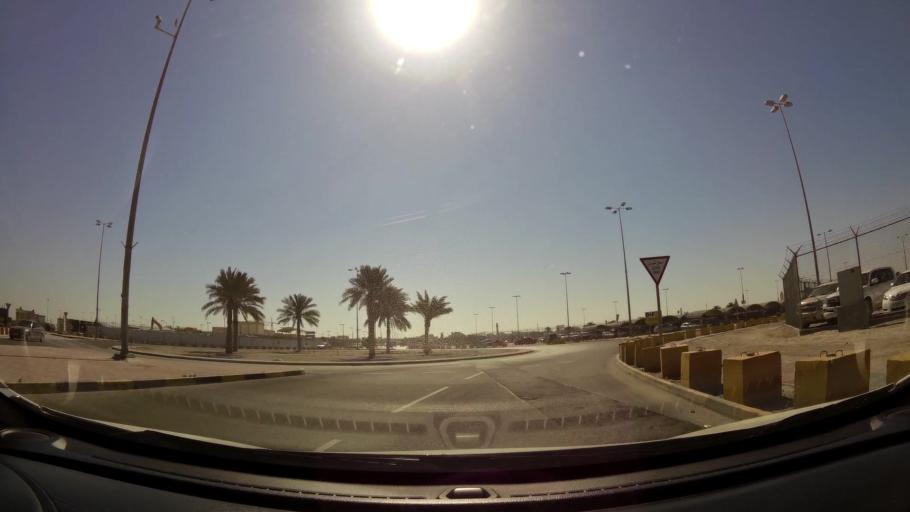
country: BH
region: Muharraq
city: Al Muharraq
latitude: 26.2650
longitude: 50.6290
